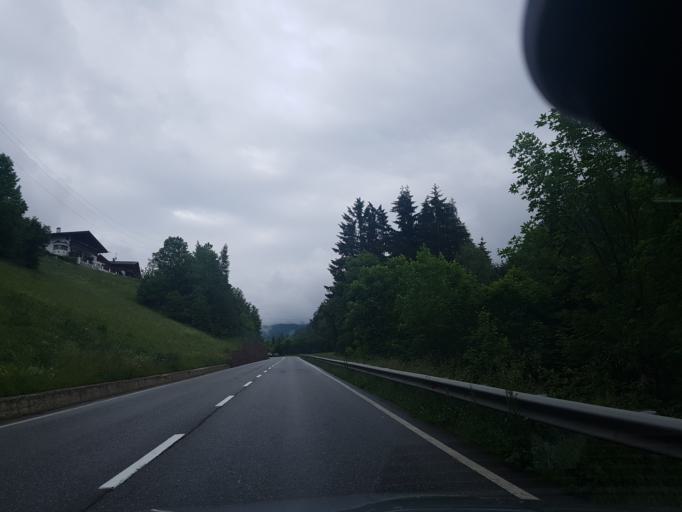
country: IT
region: Trentino-Alto Adige
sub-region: Bolzano
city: Ortisei
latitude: 46.5651
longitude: 11.6930
